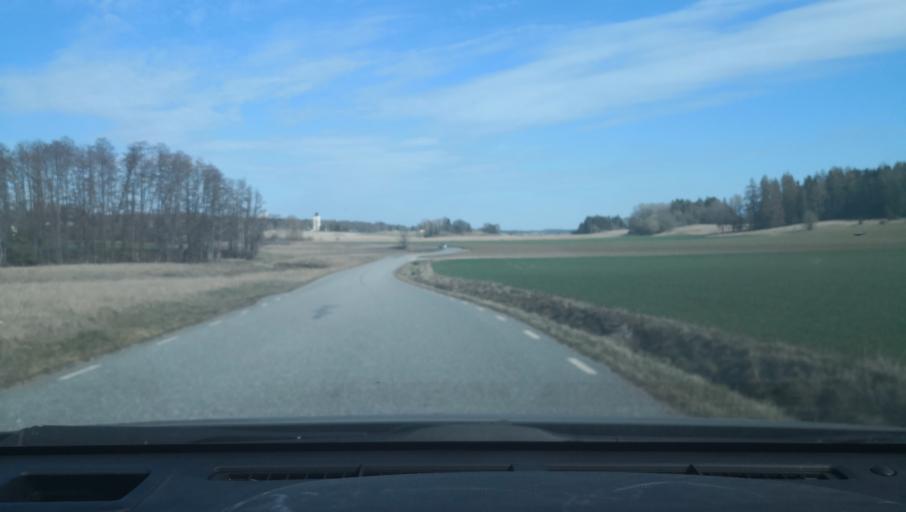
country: SE
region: Uppsala
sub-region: Enkopings Kommun
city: Irsta
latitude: 59.7711
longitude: 16.8760
